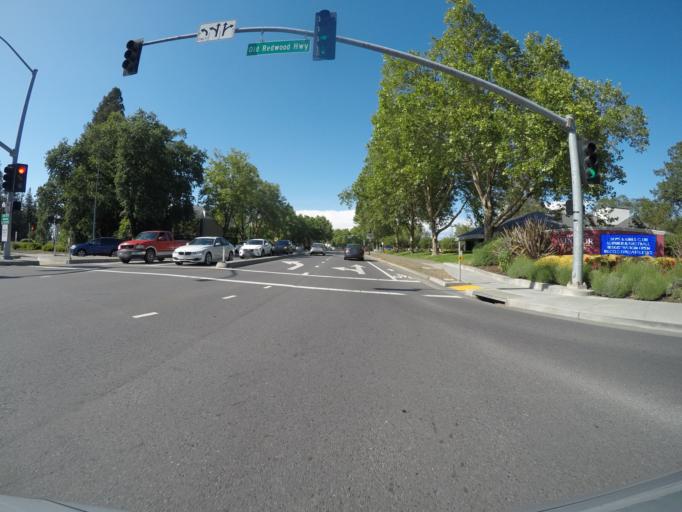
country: US
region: California
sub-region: Sonoma County
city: Windsor
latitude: 38.5465
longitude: -122.8068
